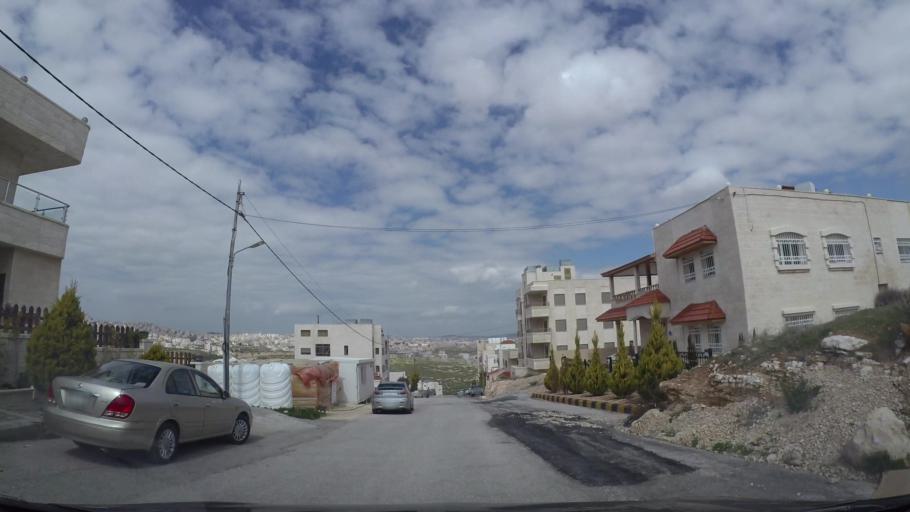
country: JO
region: Amman
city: Al Jubayhah
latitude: 32.0031
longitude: 35.9138
